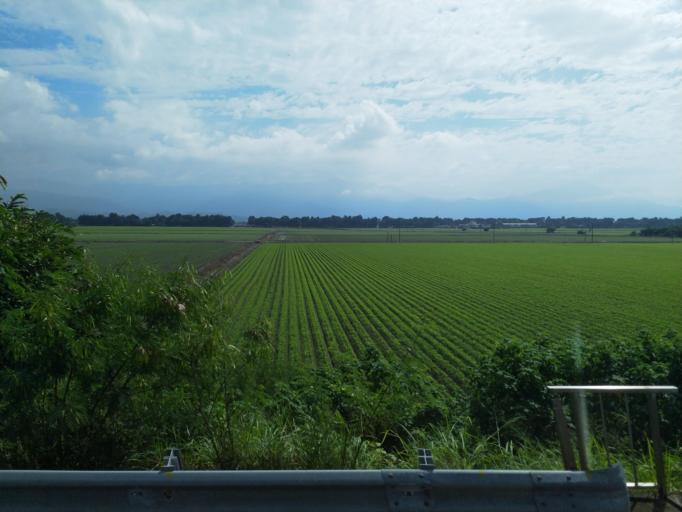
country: TW
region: Taiwan
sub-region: Pingtung
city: Pingtung
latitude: 22.8518
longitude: 120.4949
